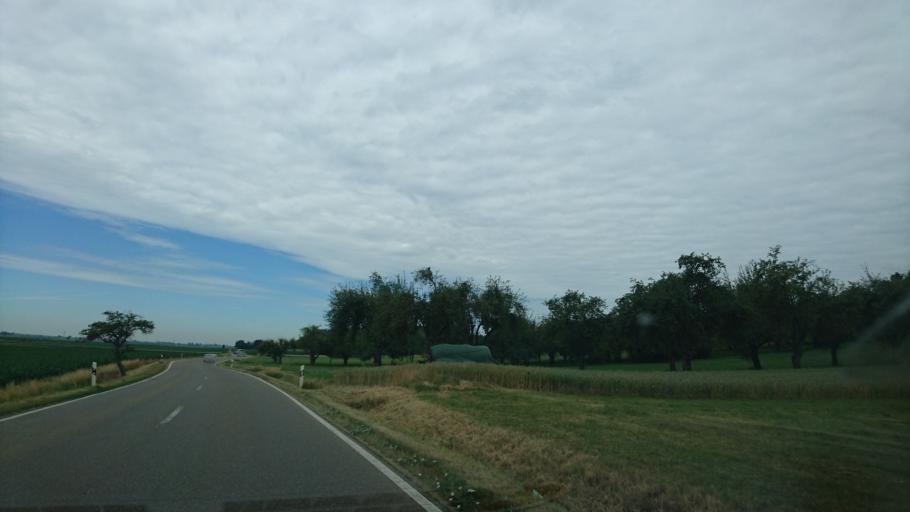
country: DE
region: Baden-Wuerttemberg
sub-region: Regierungsbezirk Stuttgart
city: Sontheim an der Brenz
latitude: 48.5493
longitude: 10.2777
